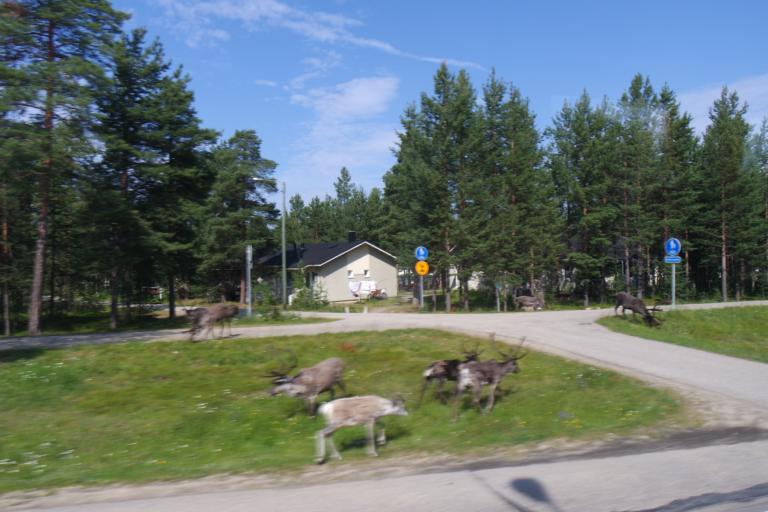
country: FI
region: Lapland
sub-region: Pohjois-Lappi
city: Ivalo
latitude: 68.6105
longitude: 27.5128
